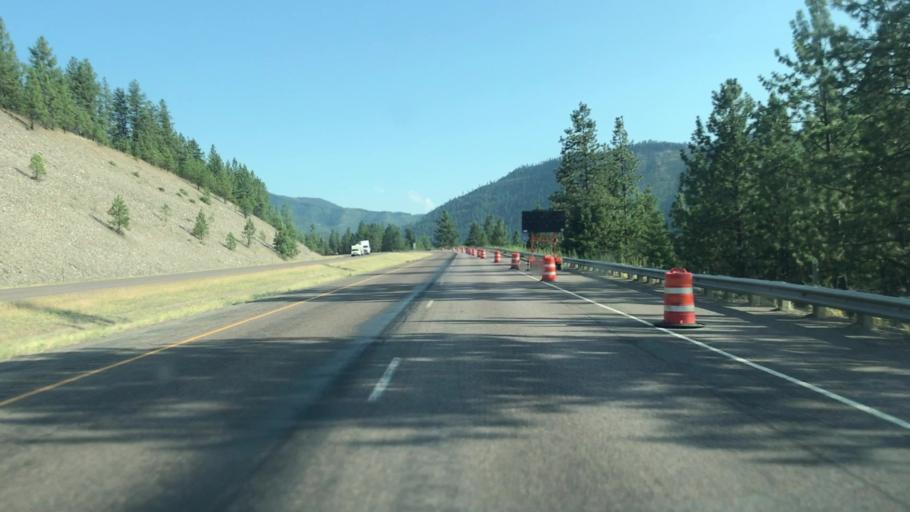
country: US
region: Montana
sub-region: Mineral County
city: Superior
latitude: 47.0206
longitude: -114.7367
